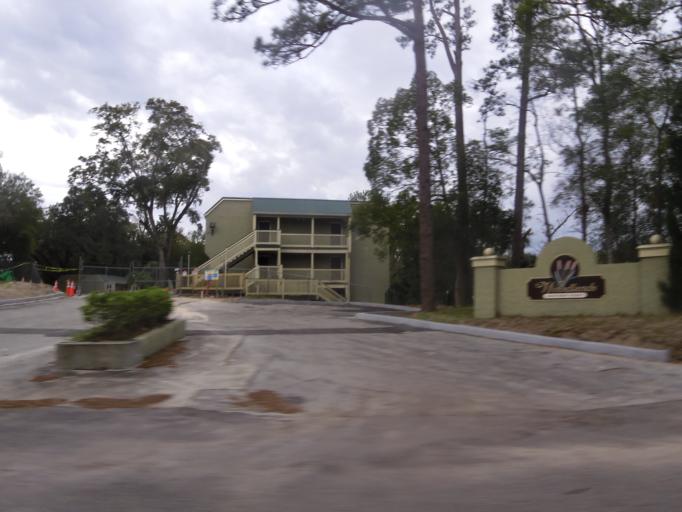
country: US
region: Florida
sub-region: Duval County
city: Jacksonville
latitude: 30.3003
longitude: -81.6133
